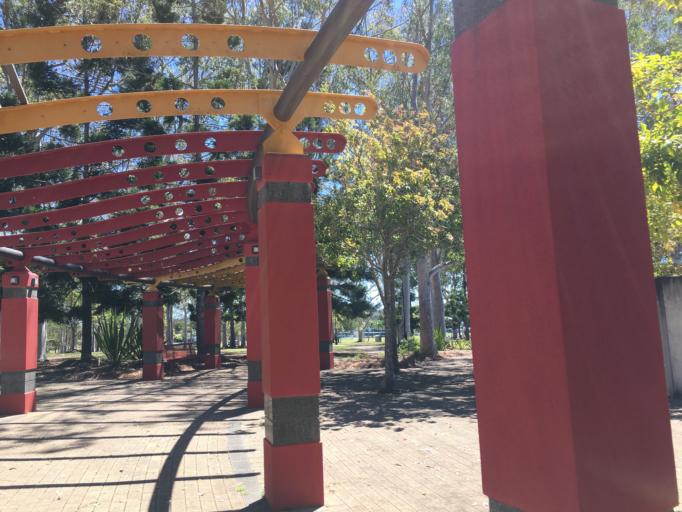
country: AU
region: Queensland
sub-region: Logan
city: Logan City
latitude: -27.6468
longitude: 153.1051
